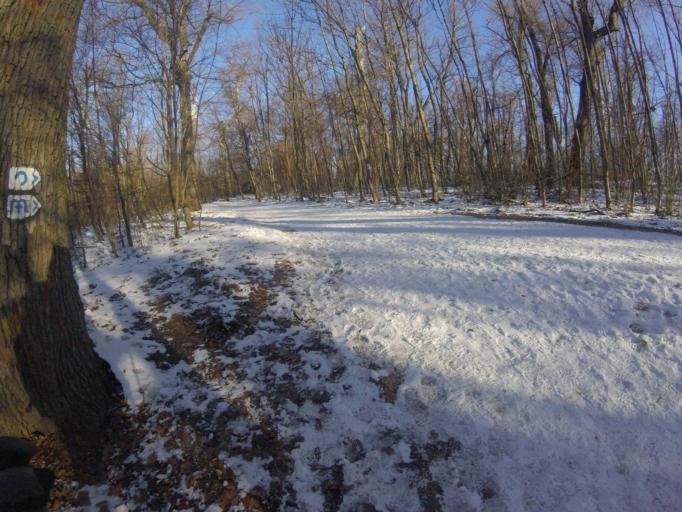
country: HU
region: Pest
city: Budakeszi
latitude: 47.5110
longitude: 18.9567
